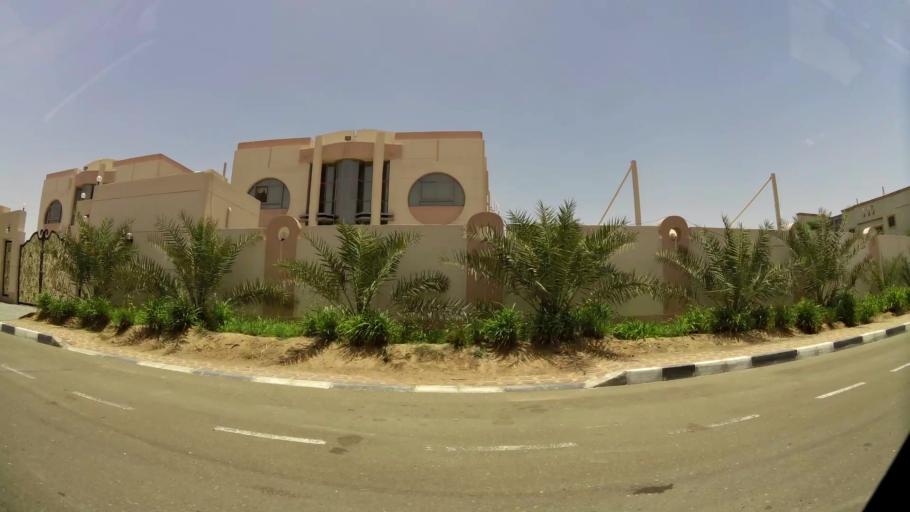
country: OM
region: Al Buraimi
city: Al Buraymi
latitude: 24.2794
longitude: 55.7307
